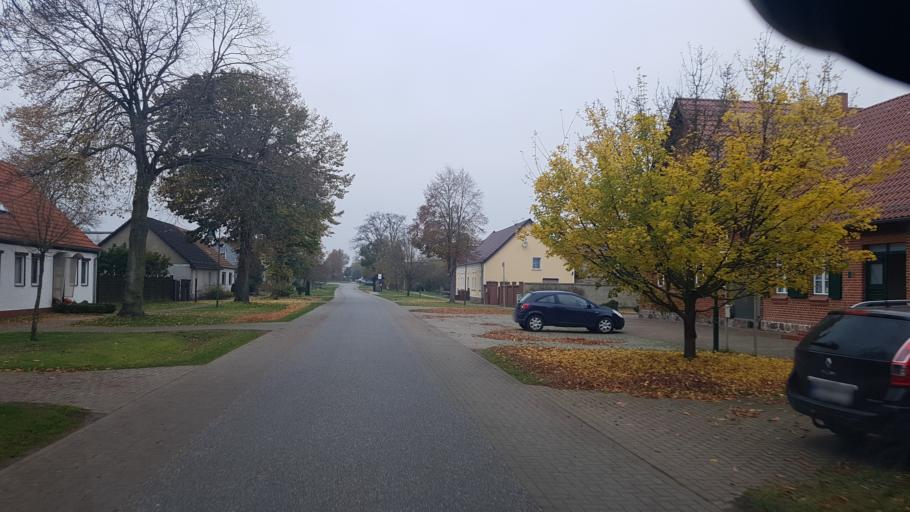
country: DE
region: Brandenburg
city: Schonermark
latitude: 52.9328
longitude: 13.1051
